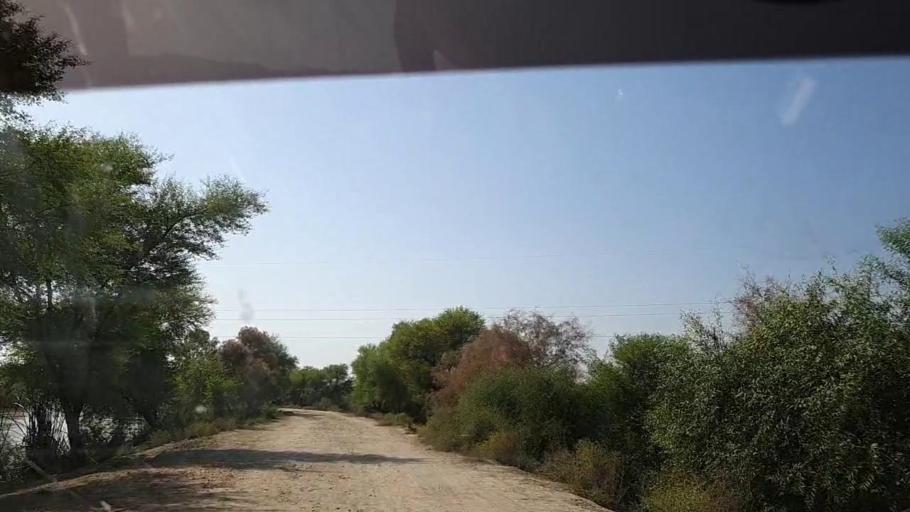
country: PK
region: Sindh
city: Ghauspur
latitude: 28.1843
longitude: 69.0802
